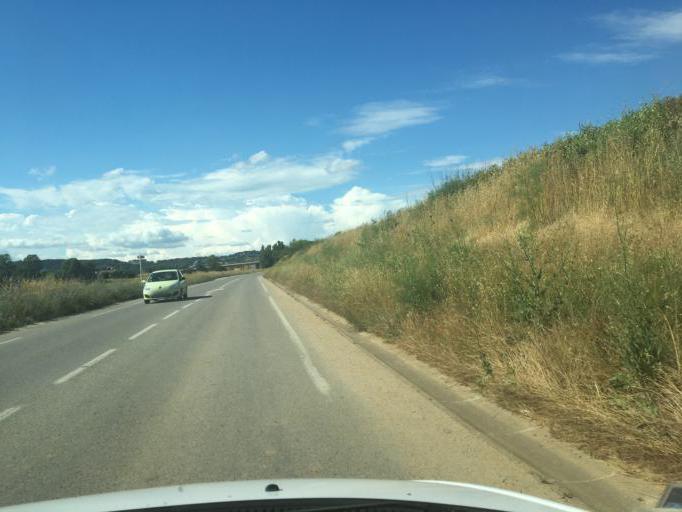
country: FR
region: Provence-Alpes-Cote d'Azur
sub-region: Departement des Bouches-du-Rhone
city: Eguilles
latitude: 43.5411
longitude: 5.3482
